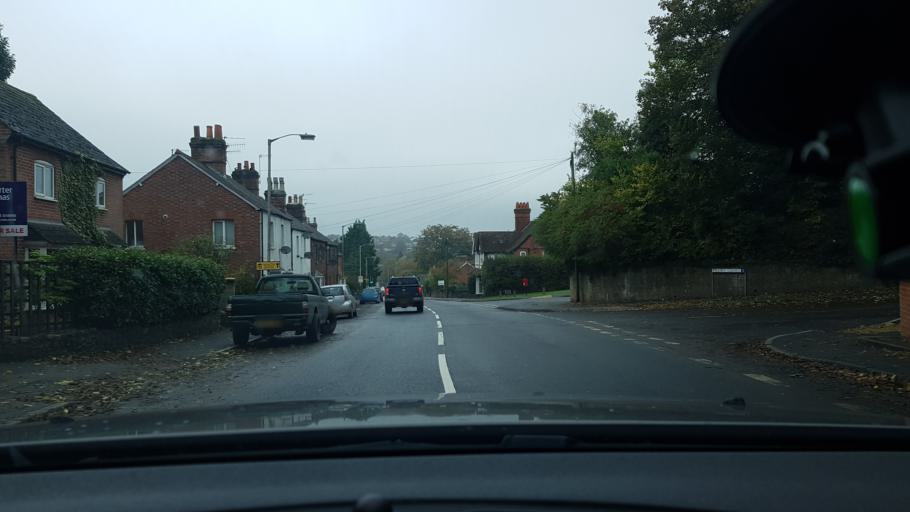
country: GB
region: England
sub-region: Wiltshire
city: Marlborough
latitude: 51.4168
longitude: -1.7234
